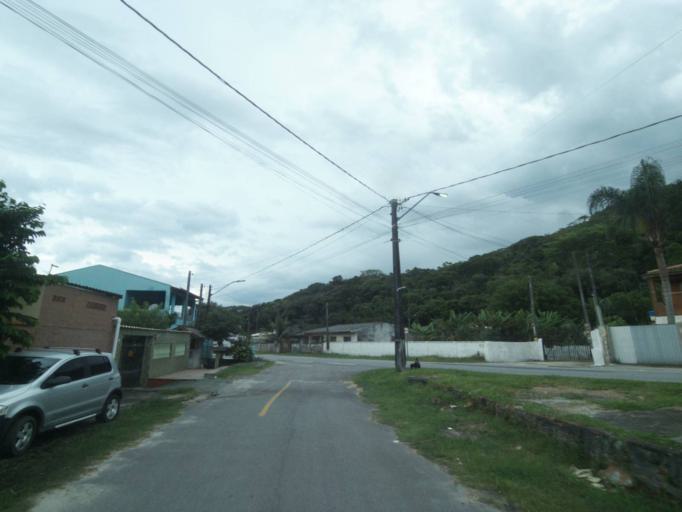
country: BR
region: Parana
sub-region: Guaratuba
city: Guaratuba
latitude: -25.8173
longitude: -48.5415
